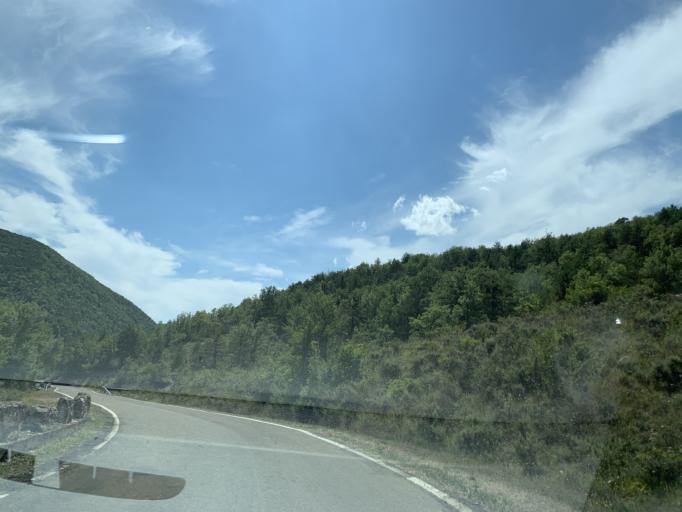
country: ES
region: Aragon
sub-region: Provincia de Huesca
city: Jasa
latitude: 42.6316
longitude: -0.6490
